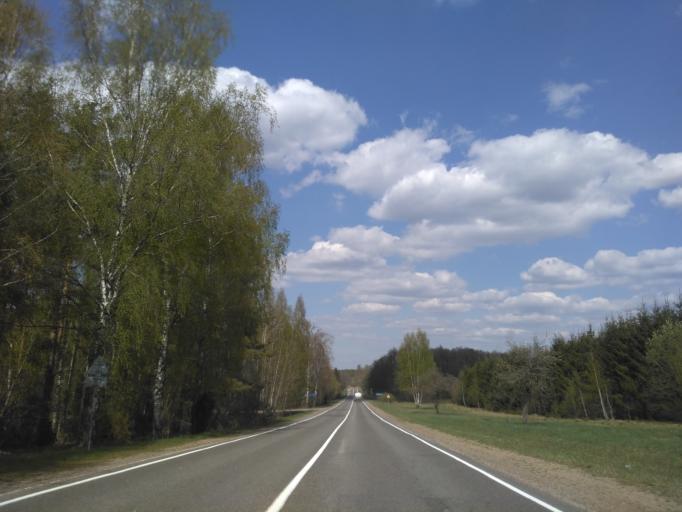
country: BY
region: Minsk
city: Myadzyel
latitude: 54.6856
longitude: 26.9220
